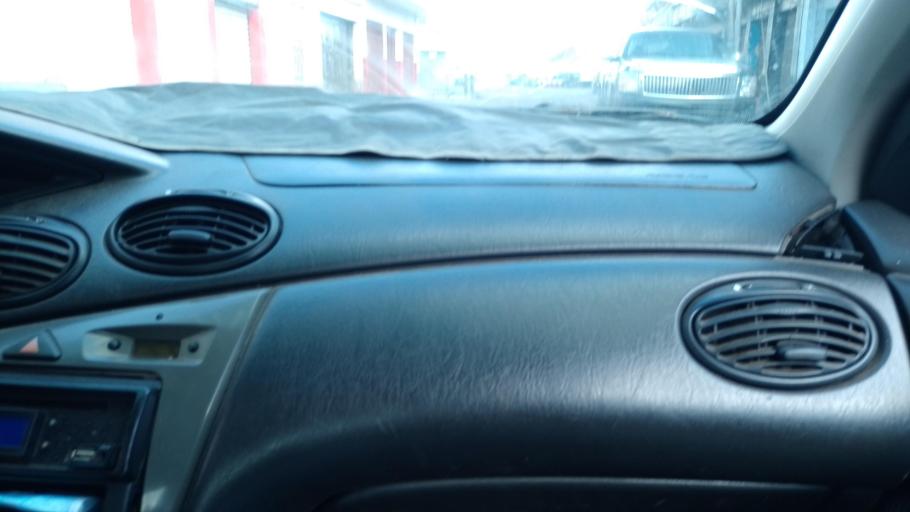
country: VE
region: Anzoategui
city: El Tigre
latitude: 8.8813
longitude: -64.2644
